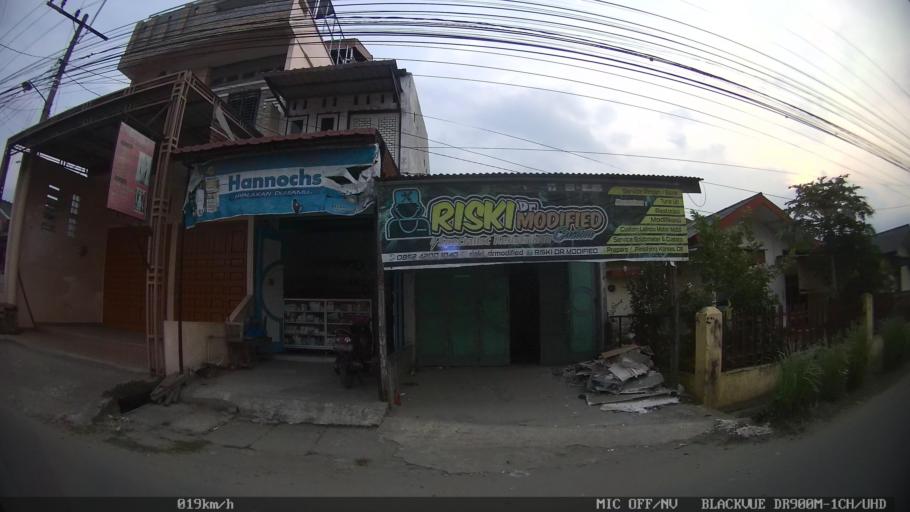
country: ID
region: North Sumatra
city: Sunggal
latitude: 3.5843
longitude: 98.5993
